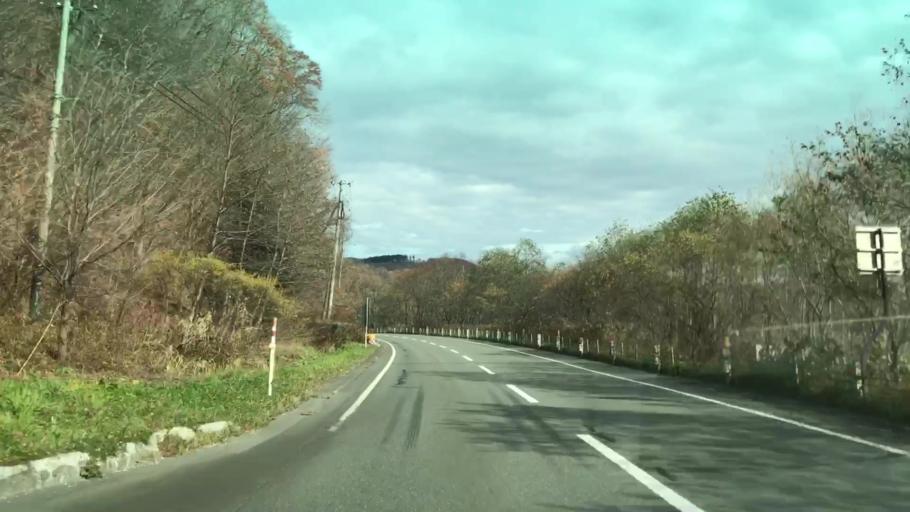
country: JP
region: Hokkaido
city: Shizunai-furukawacho
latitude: 42.7127
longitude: 142.2471
